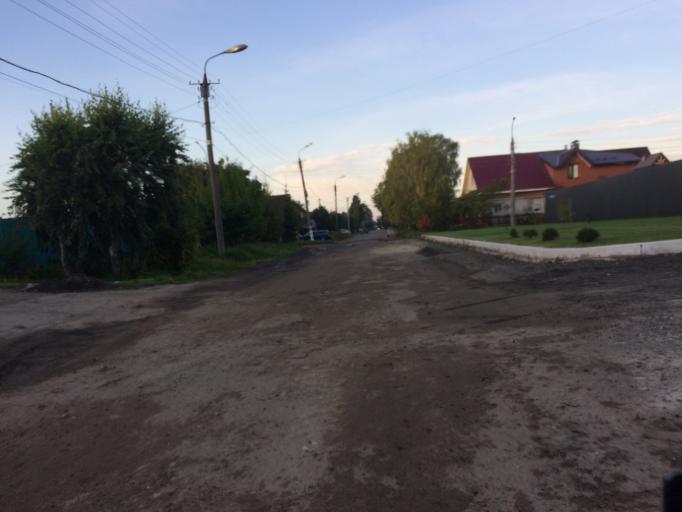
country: RU
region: Mariy-El
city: Yoshkar-Ola
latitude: 56.6542
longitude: 47.9051
